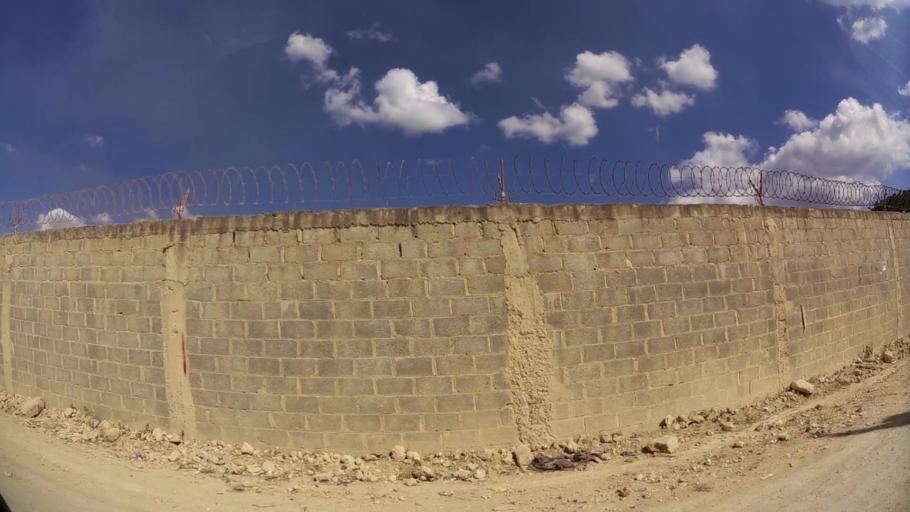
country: DO
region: Santo Domingo
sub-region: Santo Domingo
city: Santo Domingo Este
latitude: 18.4685
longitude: -69.7673
